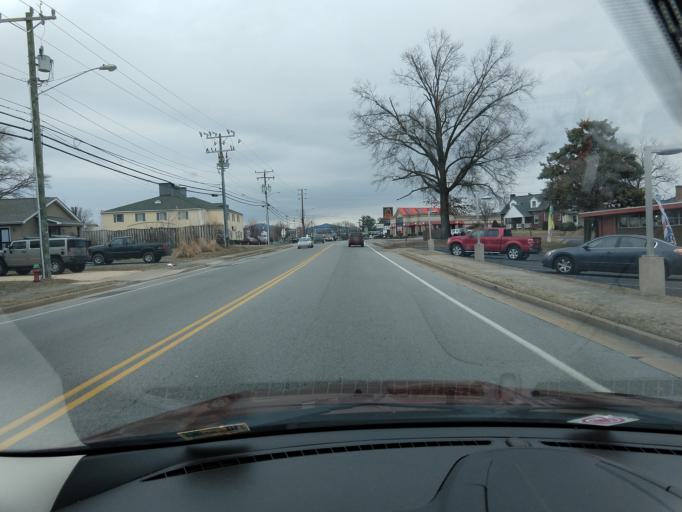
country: US
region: Virginia
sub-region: City of Waynesboro
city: Waynesboro
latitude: 38.0717
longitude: -78.9039
